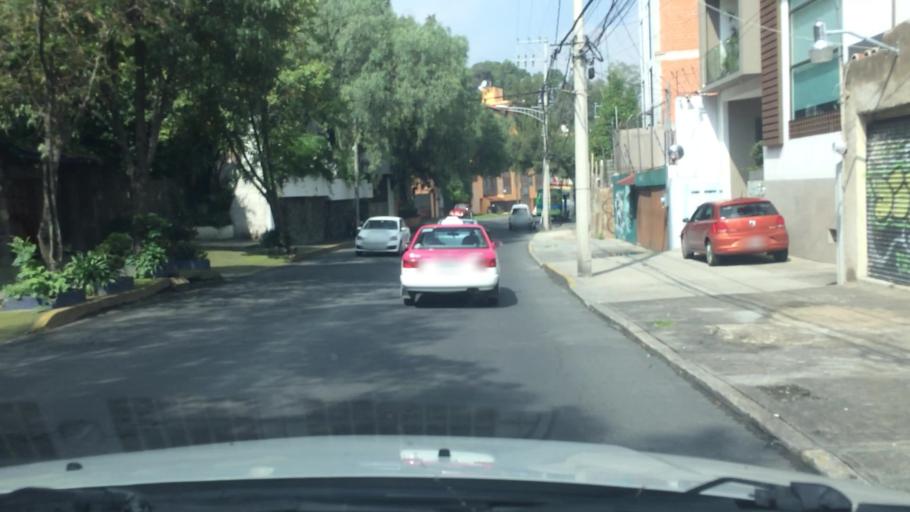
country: MX
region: Mexico City
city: Alvaro Obregon
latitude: 19.3470
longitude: -99.2048
